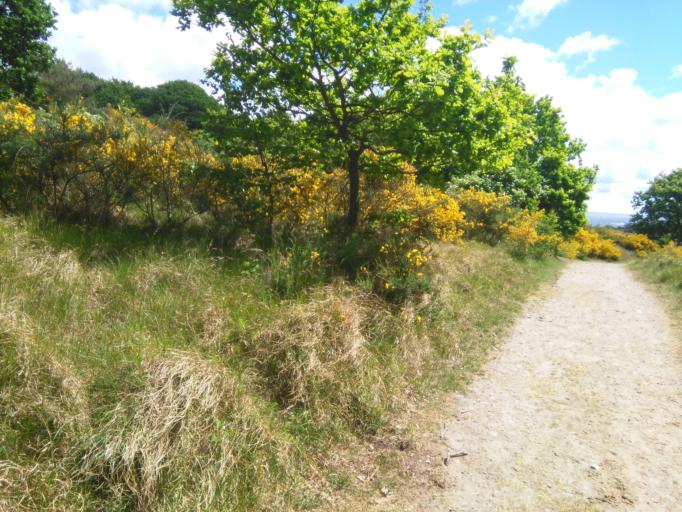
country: DK
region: Capital Region
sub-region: Bornholm Kommune
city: Ronne
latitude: 55.2932
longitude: 14.7737
